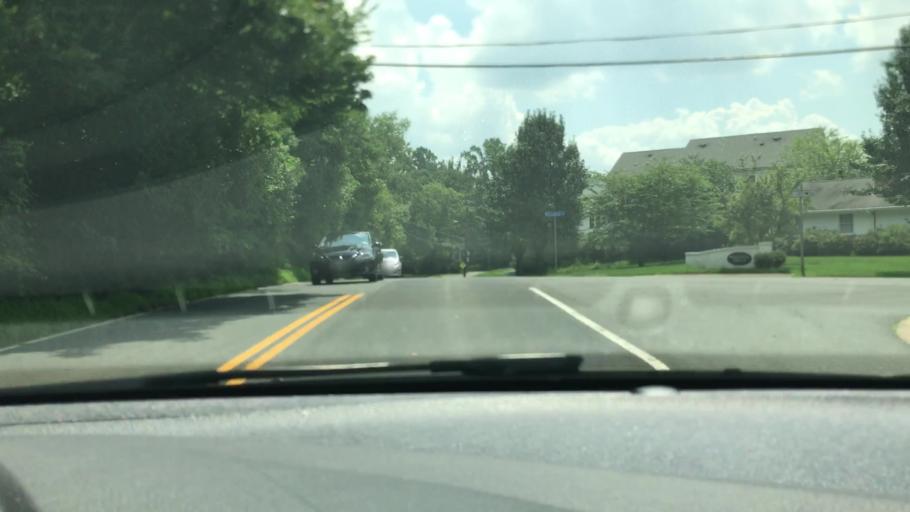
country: US
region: Maryland
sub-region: Montgomery County
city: Brookmont
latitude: 38.9288
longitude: -77.1474
